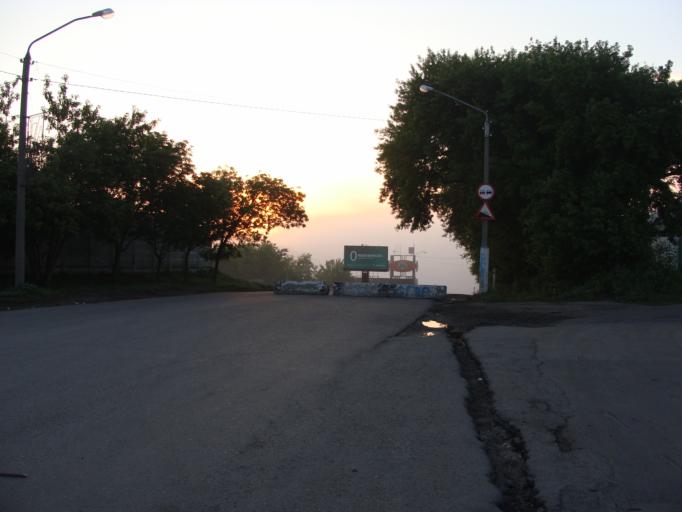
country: RU
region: Altai Krai
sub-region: Gorod Barnaulskiy
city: Barnaul
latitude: 53.3724
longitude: 83.7969
